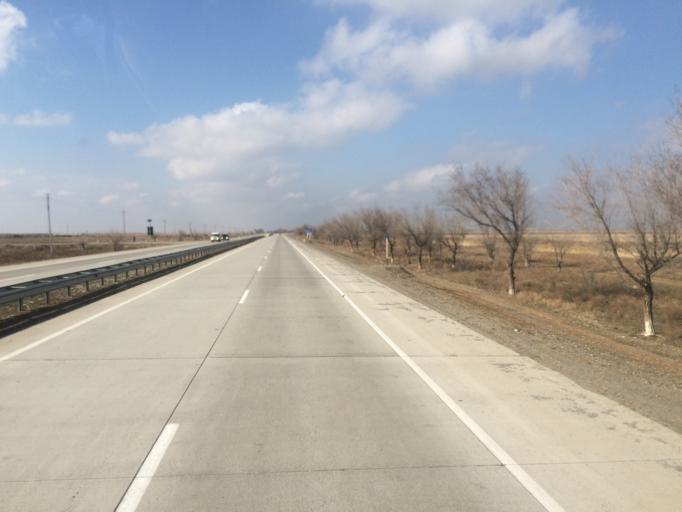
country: KZ
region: Ongtustik Qazaqstan
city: Bayaldyr
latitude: 43.0709
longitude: 68.6663
